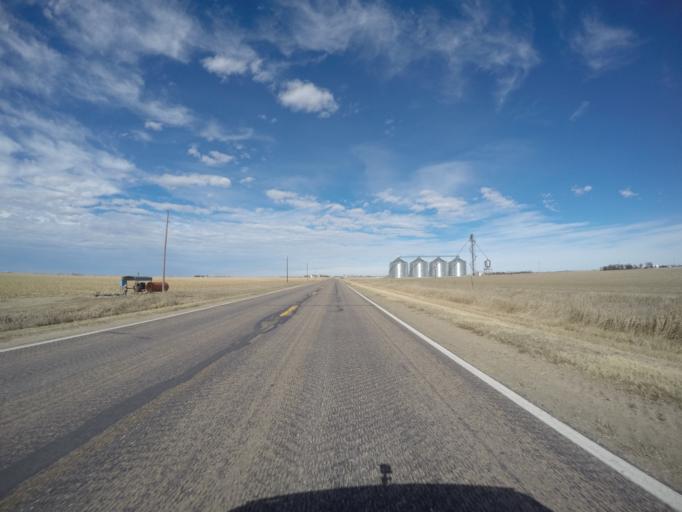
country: US
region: Nebraska
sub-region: Franklin County
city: Franklin
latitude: 40.2616
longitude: -98.9523
